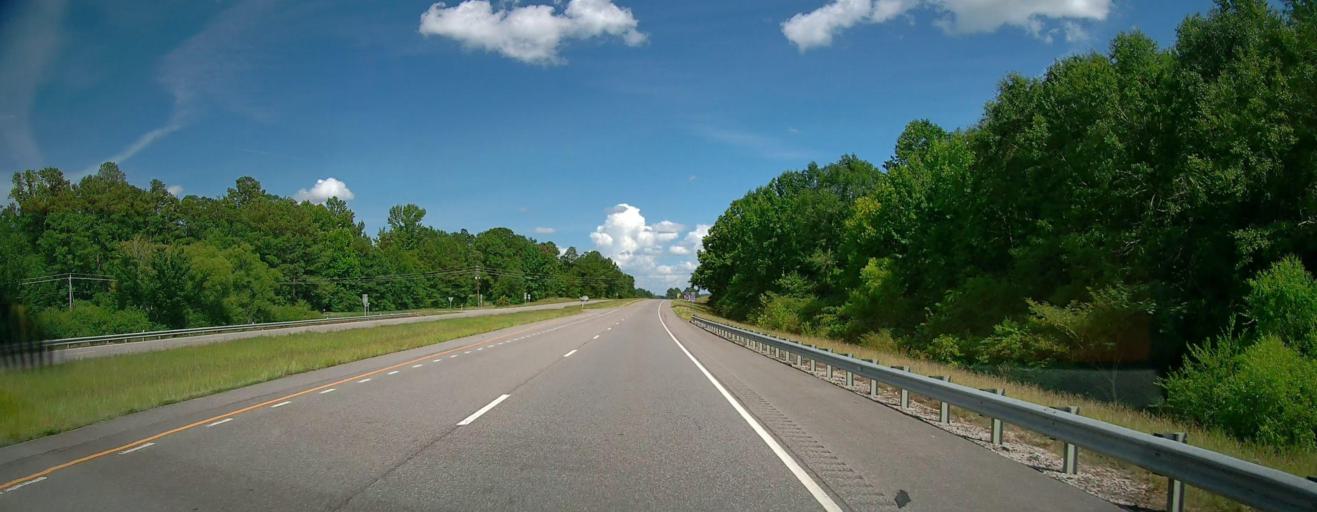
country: US
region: Alabama
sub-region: Pickens County
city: Reform
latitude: 33.3872
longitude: -88.0335
